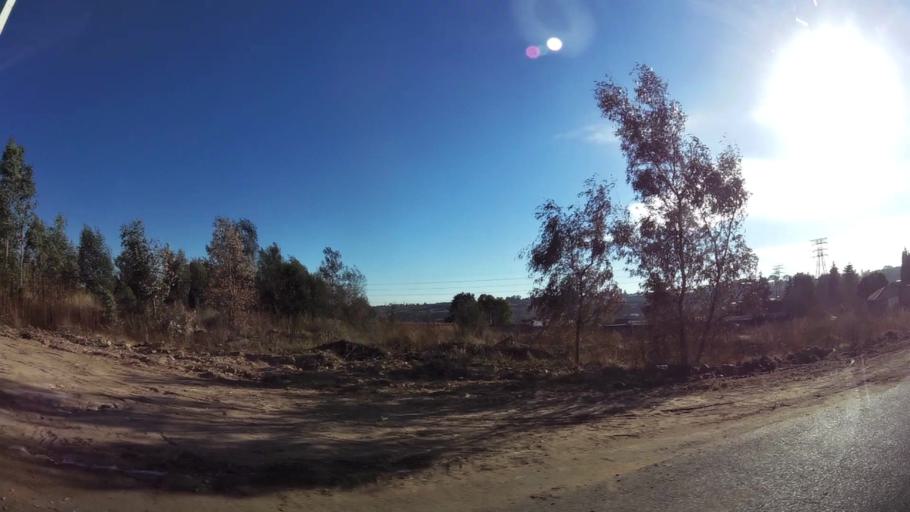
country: ZA
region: Gauteng
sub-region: West Rand District Municipality
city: Krugersdorp
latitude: -26.1193
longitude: 27.8010
